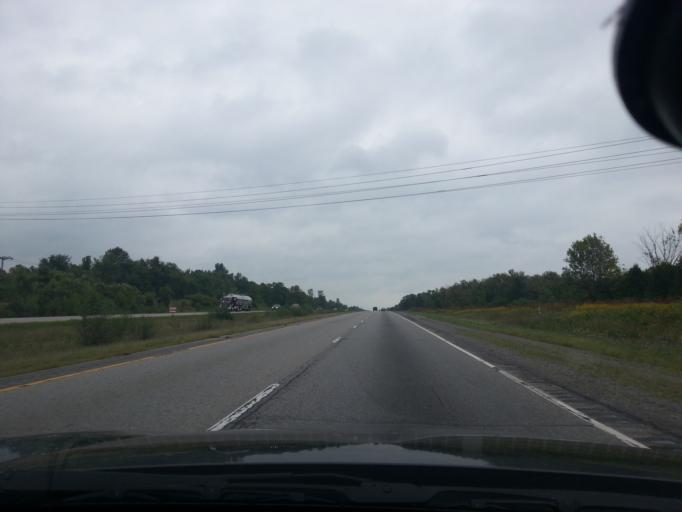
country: CA
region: Ontario
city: Prescott
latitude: 44.6718
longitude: -75.6032
